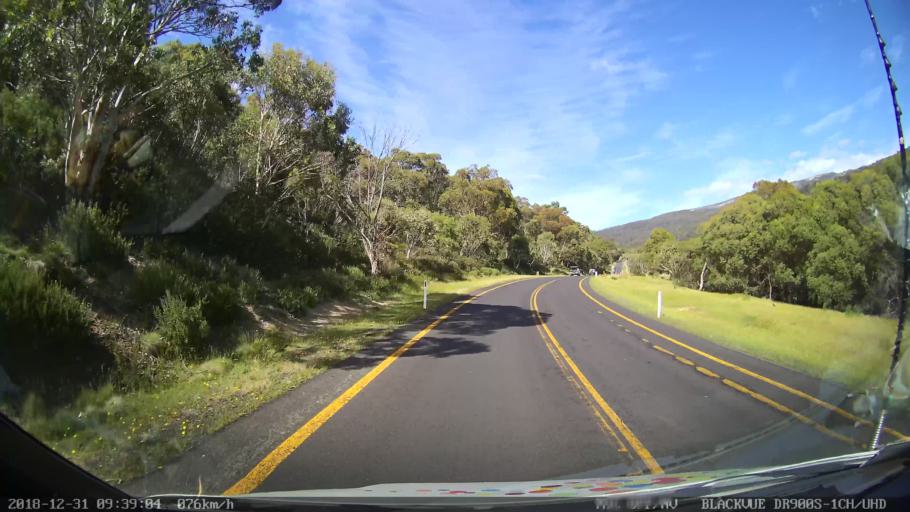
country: AU
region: New South Wales
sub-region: Snowy River
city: Jindabyne
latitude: -36.4778
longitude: 148.3598
